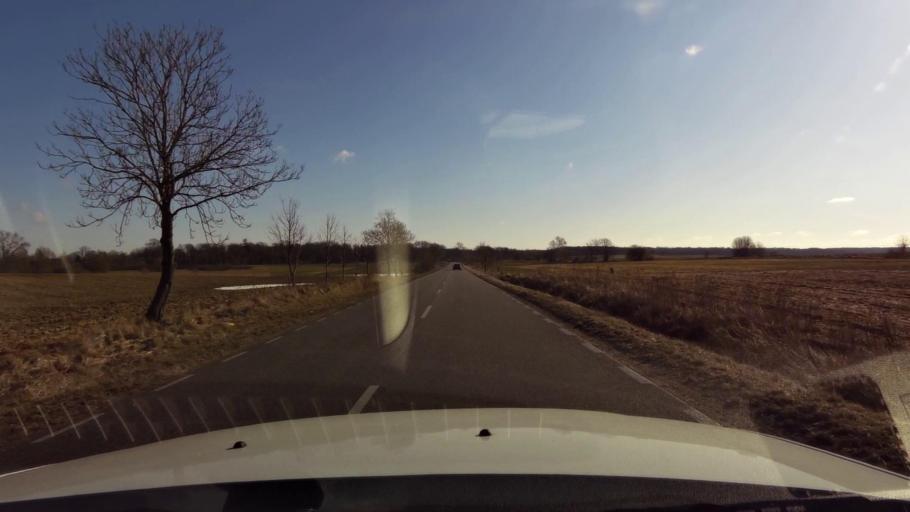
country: PL
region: West Pomeranian Voivodeship
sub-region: Powiat mysliborski
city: Barlinek
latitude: 52.9864
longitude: 15.1115
